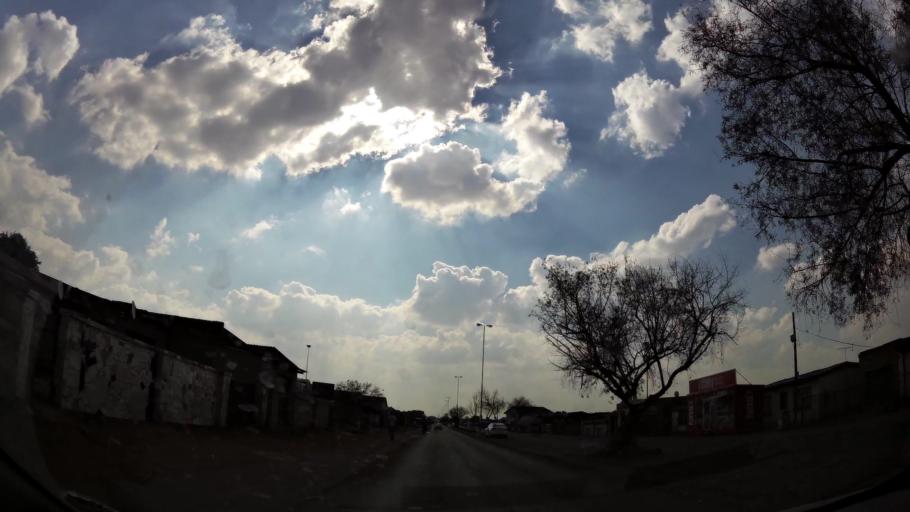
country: ZA
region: Gauteng
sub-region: Ekurhuleni Metropolitan Municipality
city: Germiston
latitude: -26.3502
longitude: 28.1498
